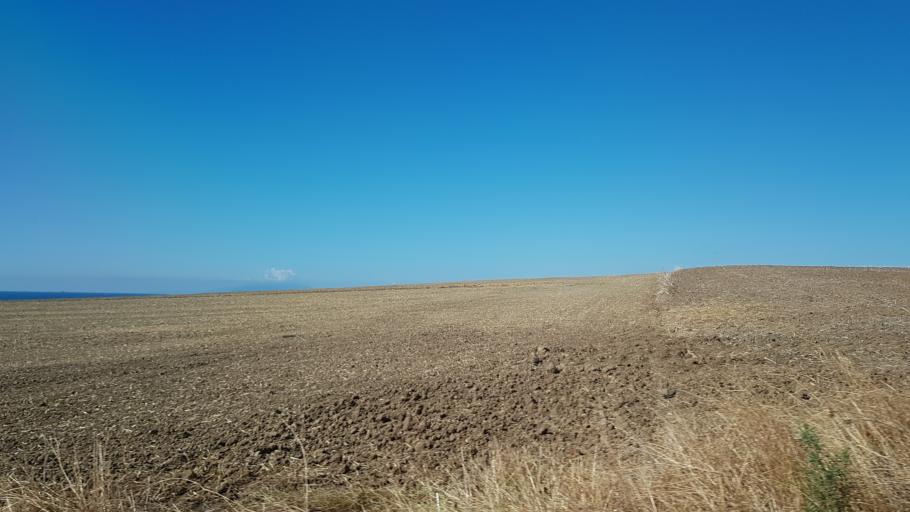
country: TR
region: Tekirdag
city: Corlu
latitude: 41.0183
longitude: 27.8064
